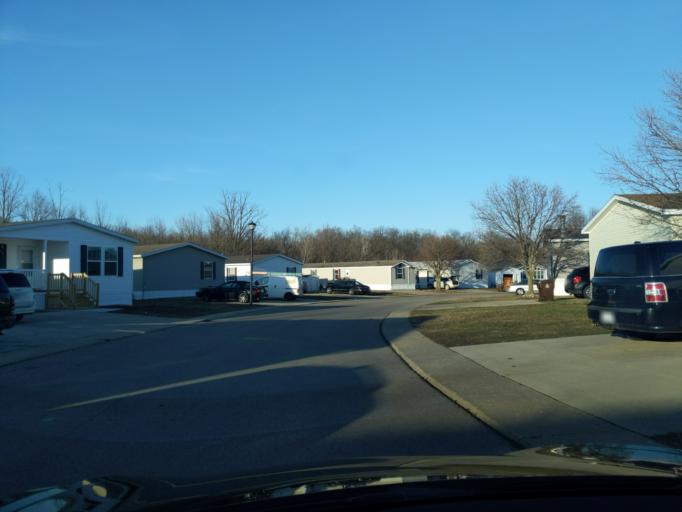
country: US
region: Michigan
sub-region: Jackson County
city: Jackson
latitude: 42.2824
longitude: -84.4784
